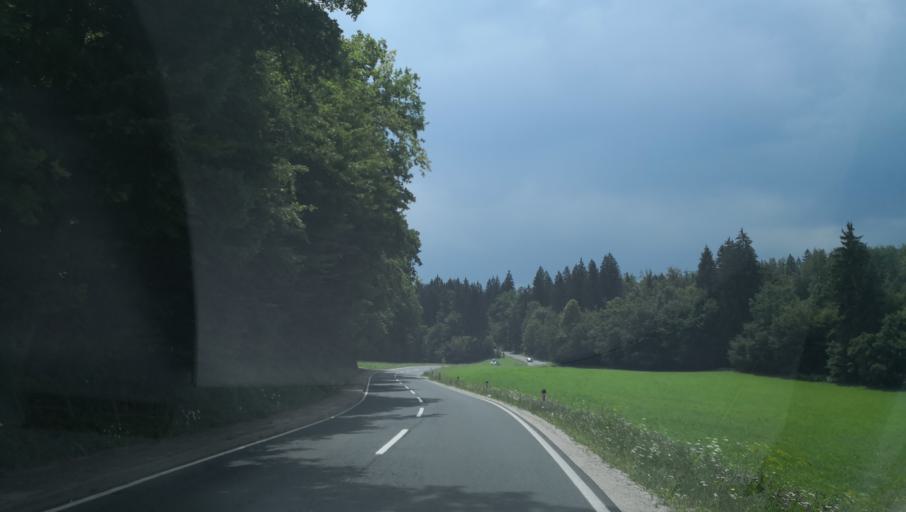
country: SI
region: Ivancna Gorica
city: Ivancna Gorica
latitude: 45.8989
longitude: 14.7993
